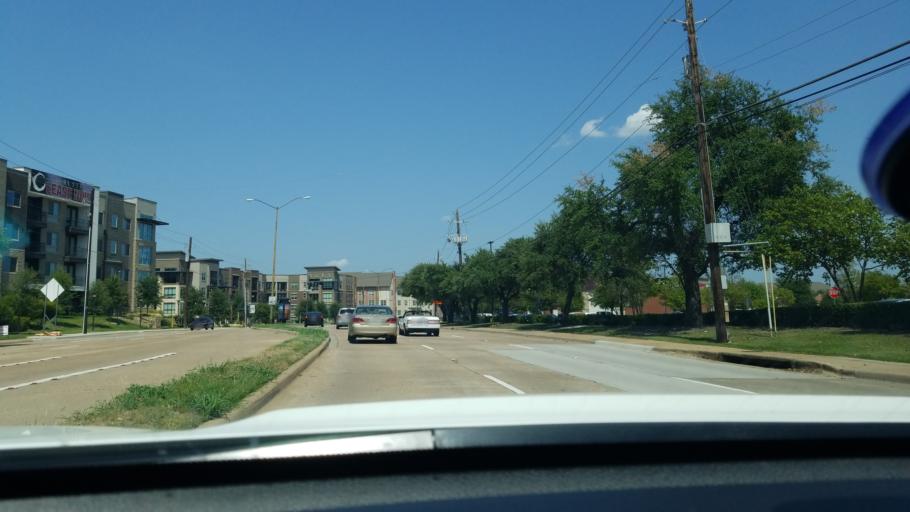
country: US
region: Texas
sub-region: Dallas County
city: Addison
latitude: 32.9601
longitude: -96.8182
